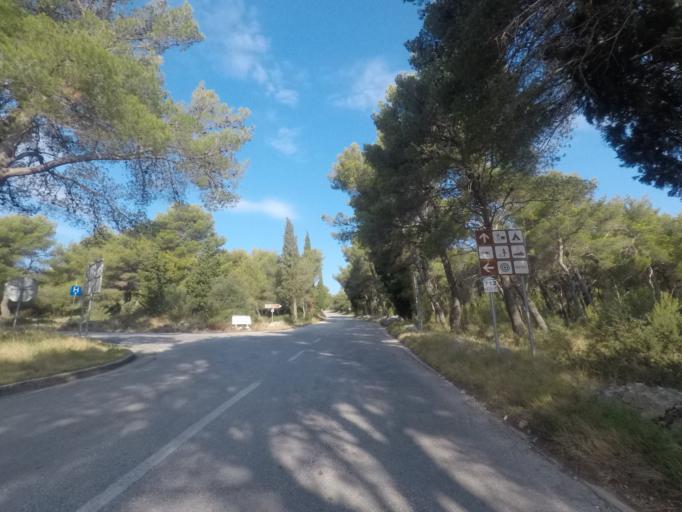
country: HR
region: Splitsko-Dalmatinska
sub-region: Grad Hvar
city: Hvar
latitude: 43.1761
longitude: 16.4389
